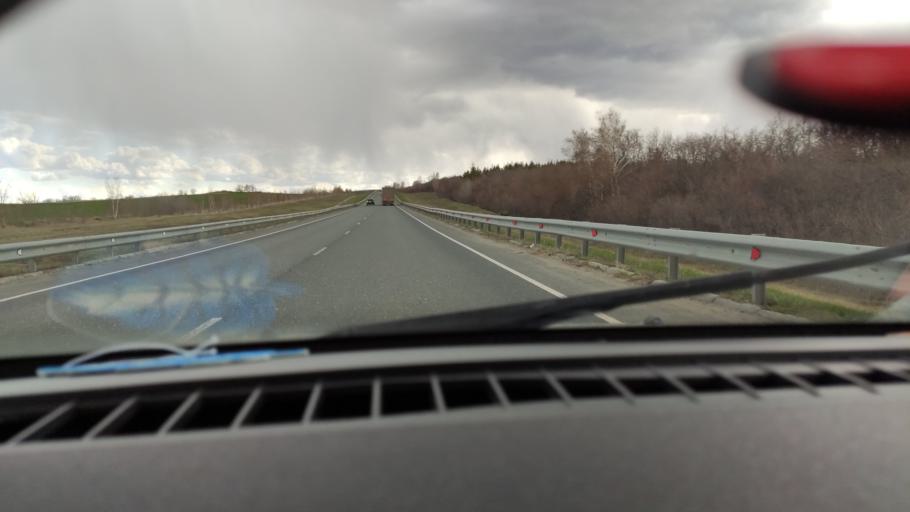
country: RU
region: Saratov
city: Balakovo
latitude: 52.1705
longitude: 47.8301
